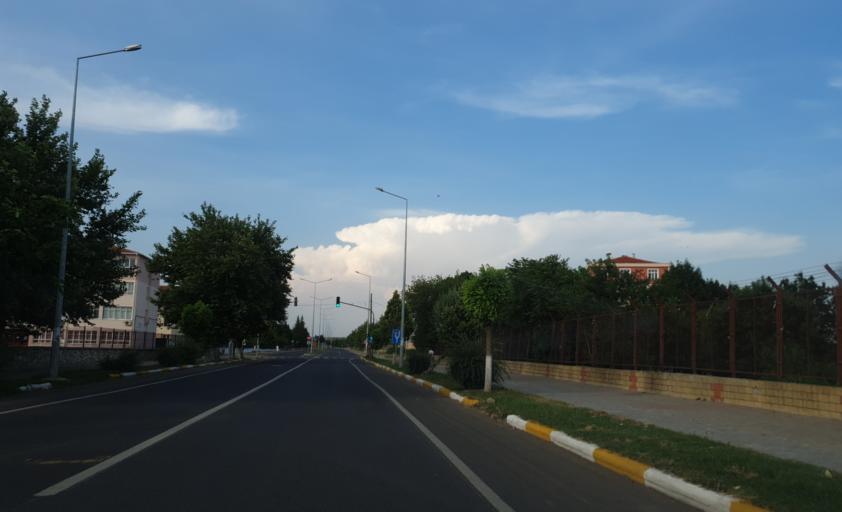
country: TR
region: Tekirdag
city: Hayrabolu
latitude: 41.2198
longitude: 27.1113
